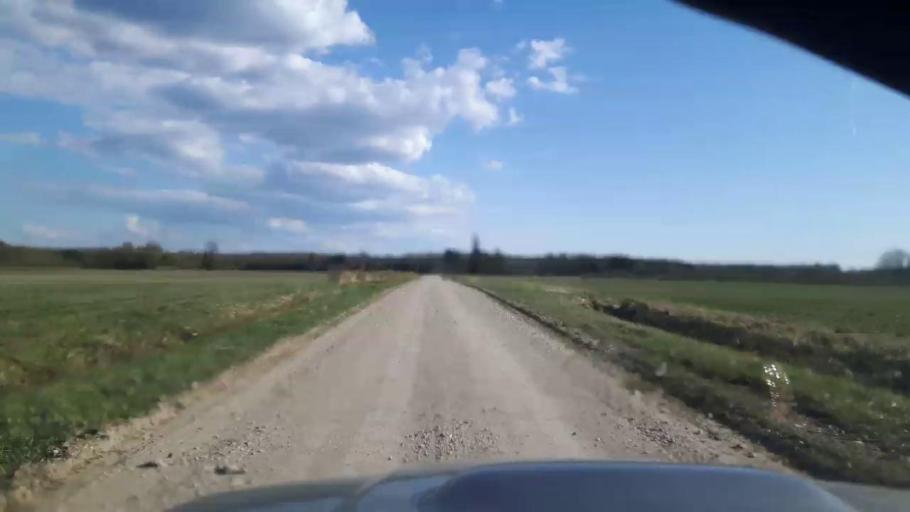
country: EE
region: Paernumaa
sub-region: Tootsi vald
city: Tootsi
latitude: 58.4376
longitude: 24.8560
